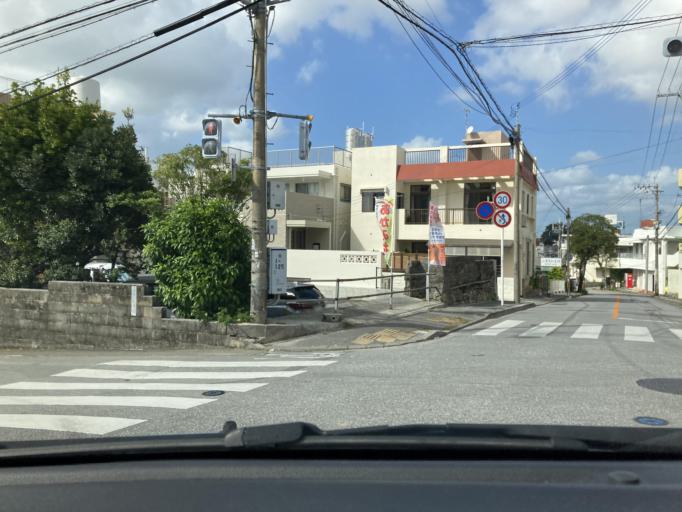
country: JP
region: Okinawa
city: Naha-shi
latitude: 26.2053
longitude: 127.7099
